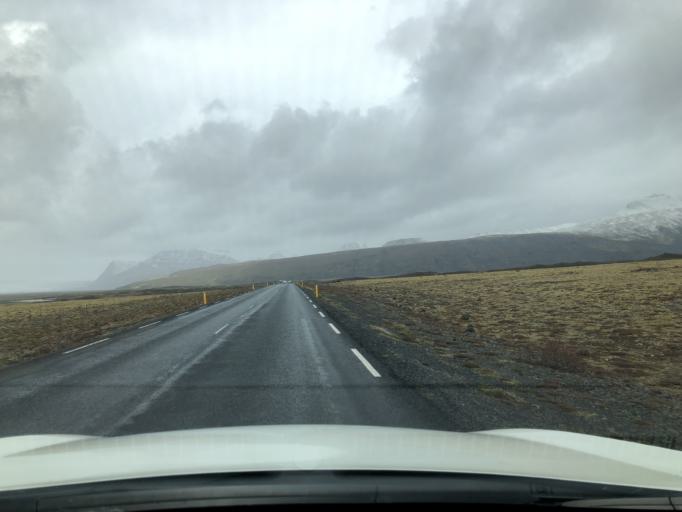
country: IS
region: East
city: Hoefn
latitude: 63.9993
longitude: -16.9138
